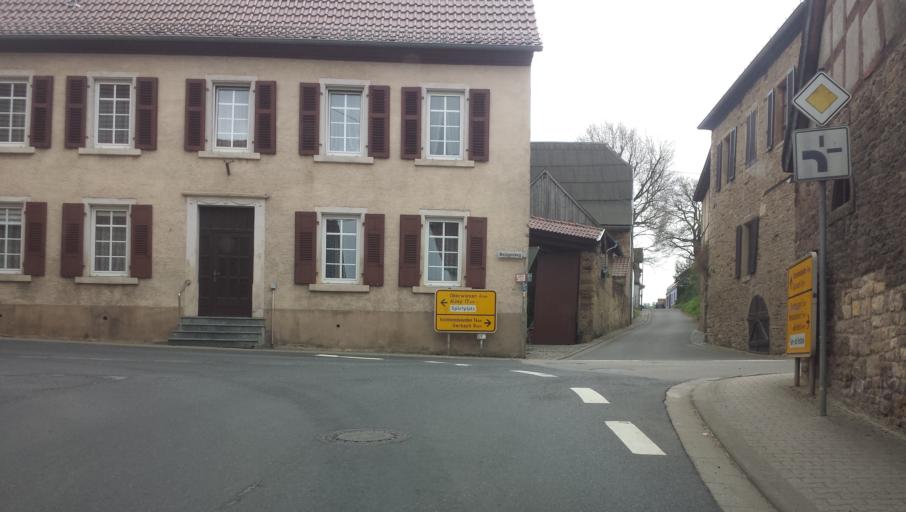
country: DE
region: Rheinland-Pfalz
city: Kriegsfeld
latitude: 49.7084
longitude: 7.9178
